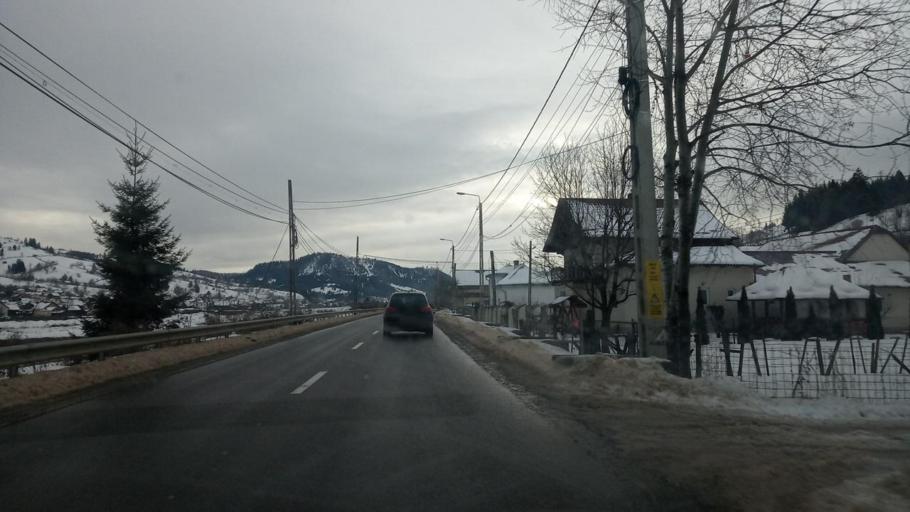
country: RO
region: Suceava
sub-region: Comuna Frasin
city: Frasin
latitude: 47.5108
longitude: 25.7988
